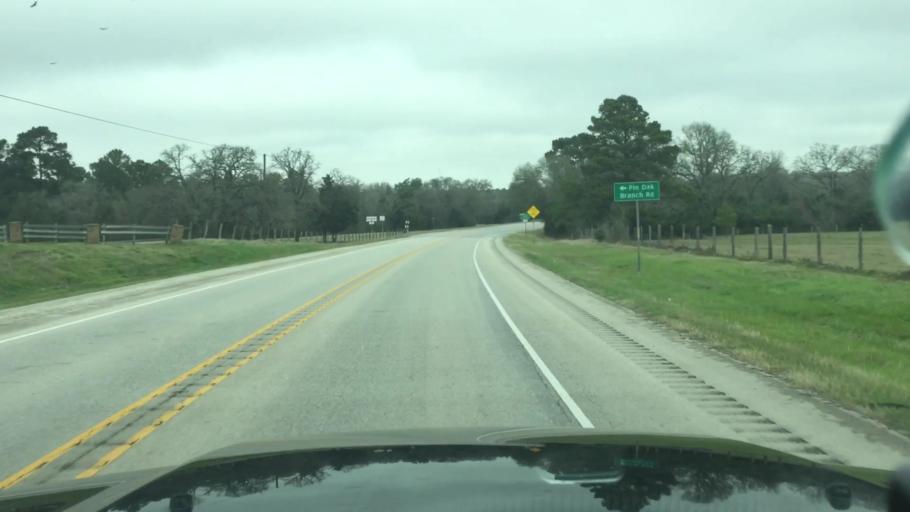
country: US
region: Texas
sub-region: Lee County
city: Giddings
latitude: 30.0810
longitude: -96.9172
